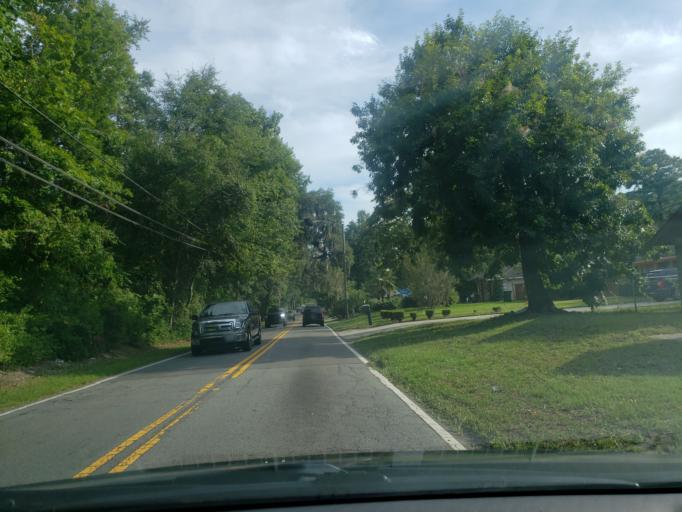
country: US
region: Georgia
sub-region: Chatham County
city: Montgomery
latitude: 31.9634
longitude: -81.1358
